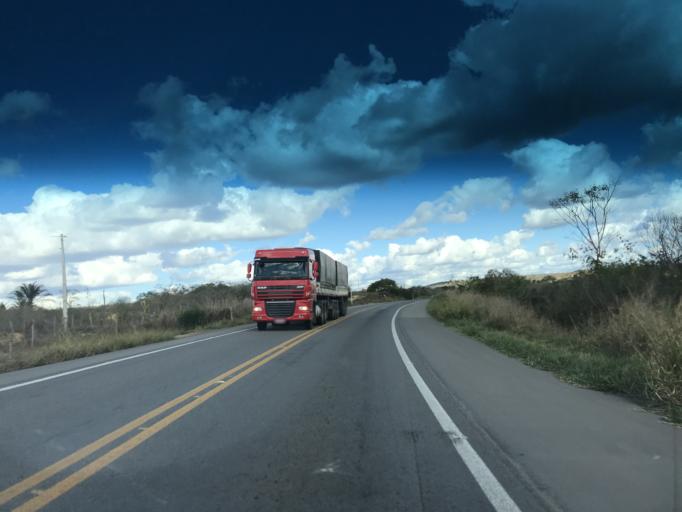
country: BR
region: Bahia
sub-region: Andarai
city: Vera Cruz
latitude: -12.4605
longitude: -40.9810
